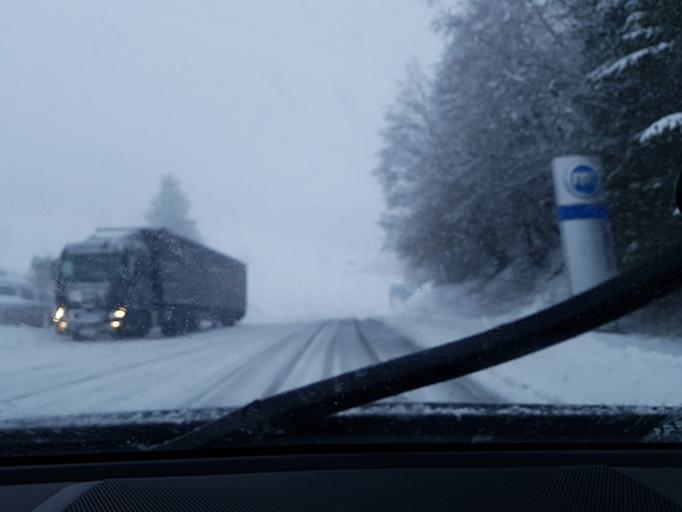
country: AT
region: Salzburg
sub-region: Politischer Bezirk Hallein
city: Abtenau
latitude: 47.5626
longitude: 13.3797
